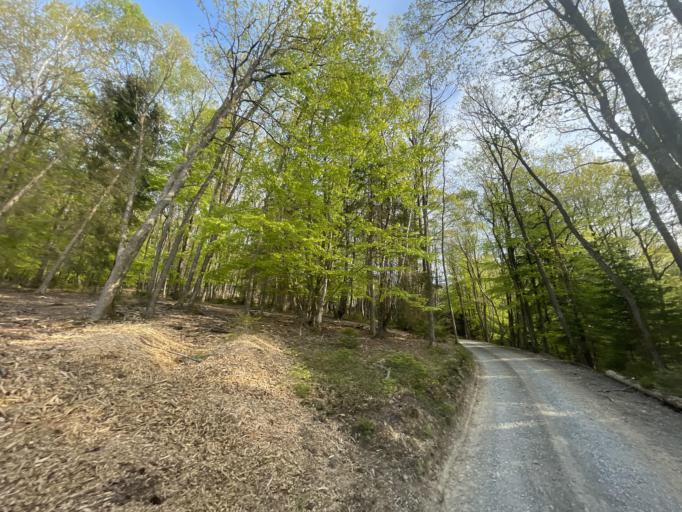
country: DE
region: North Rhine-Westphalia
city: Werdohl
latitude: 51.2127
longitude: 7.8086
